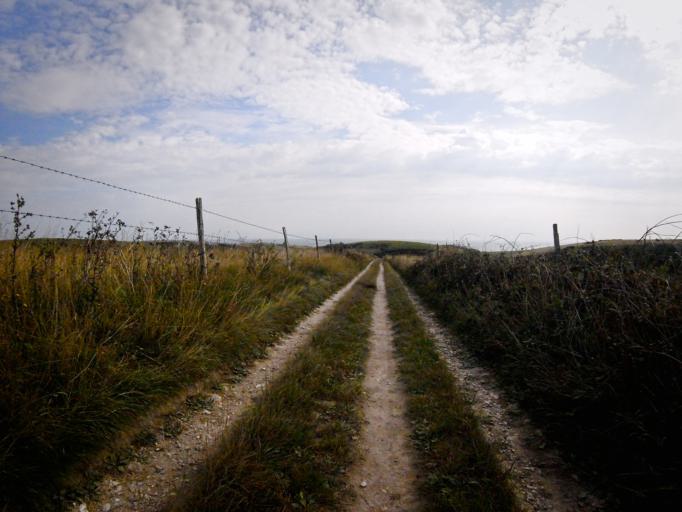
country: GB
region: England
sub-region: Brighton and Hove
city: Rottingdean
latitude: 50.8272
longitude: -0.0866
